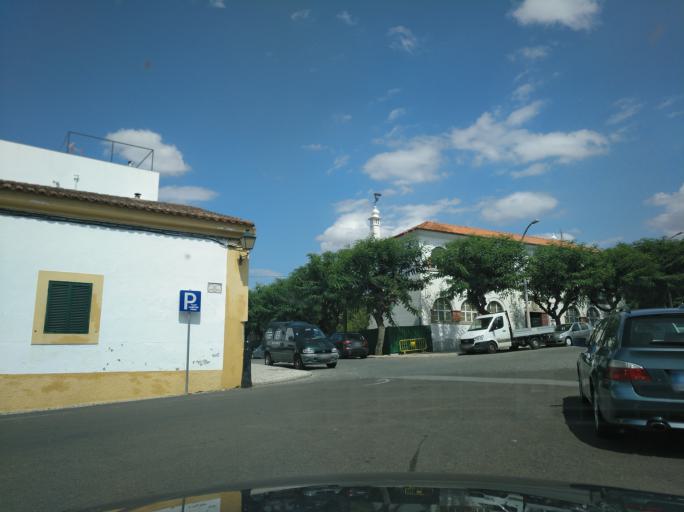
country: PT
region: Portalegre
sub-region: Campo Maior
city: Campo Maior
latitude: 39.0139
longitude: -7.0704
